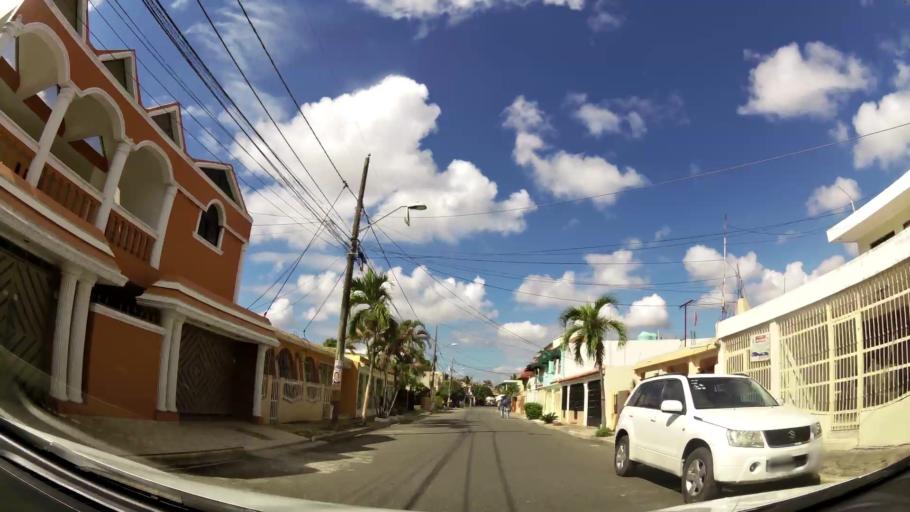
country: DO
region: Santo Domingo
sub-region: Santo Domingo
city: Santo Domingo Este
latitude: 18.5099
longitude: -69.8462
